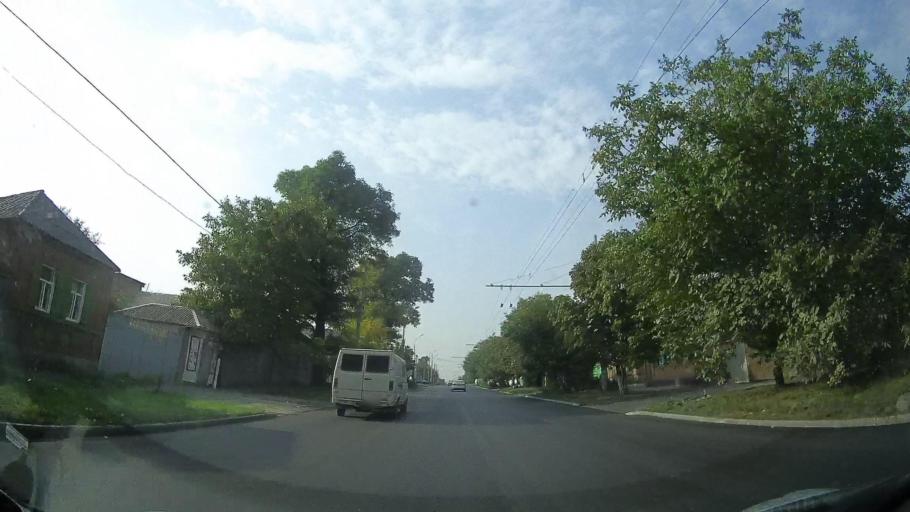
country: RU
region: Rostov
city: Rostov-na-Donu
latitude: 47.2542
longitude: 39.7028
